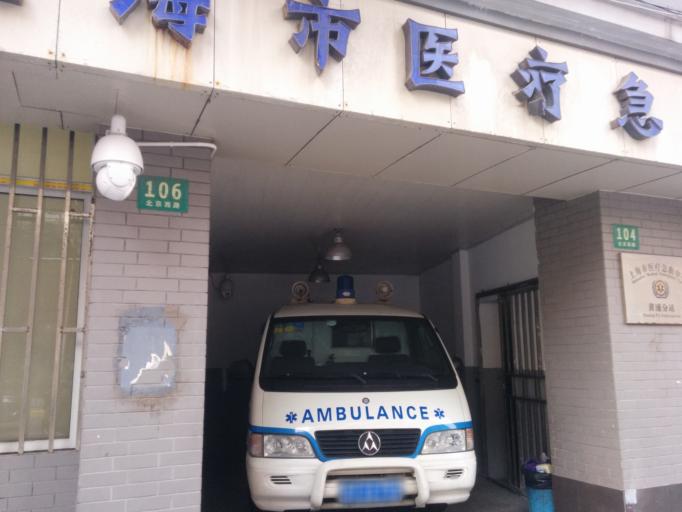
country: CN
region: Shanghai Shi
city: Shanghai
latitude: 31.2385
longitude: 121.4670
